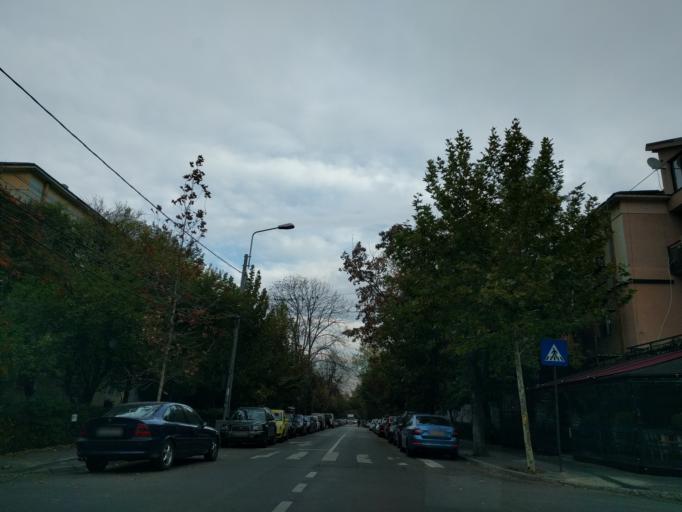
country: RO
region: Bucuresti
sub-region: Municipiul Bucuresti
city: Bucharest
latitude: 44.4266
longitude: 26.1439
